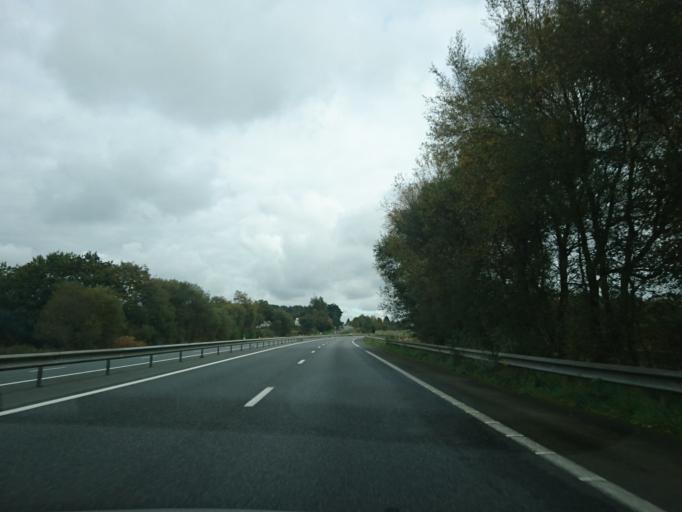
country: FR
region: Brittany
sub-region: Departement du Finistere
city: Guerlesquin
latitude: 48.5672
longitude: -3.5542
